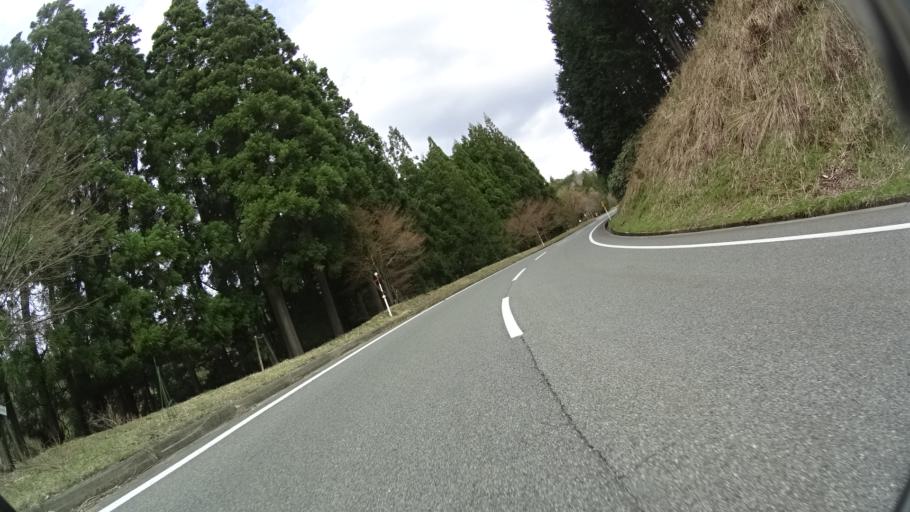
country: JP
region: Hyogo
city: Toyooka
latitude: 35.5074
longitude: 134.8943
